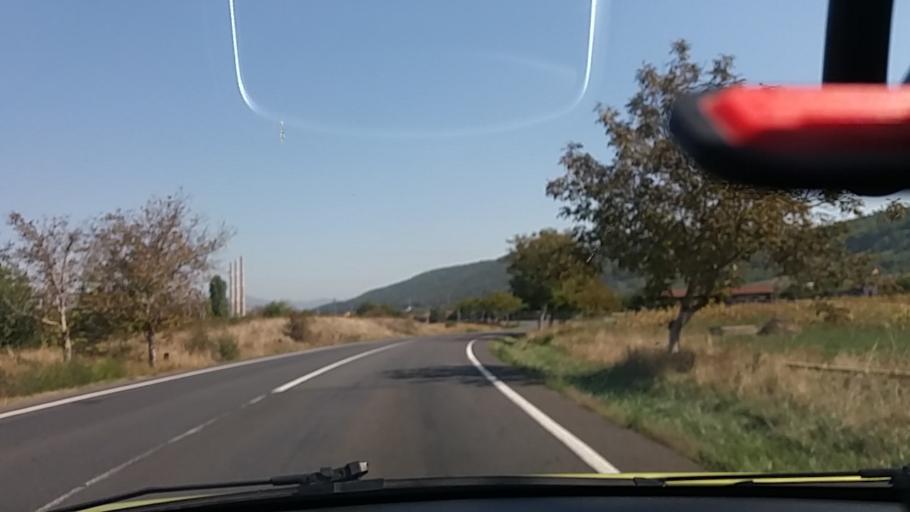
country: RO
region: Hunedoara
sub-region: Comuna Branisca
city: Branisca
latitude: 45.9044
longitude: 22.7951
